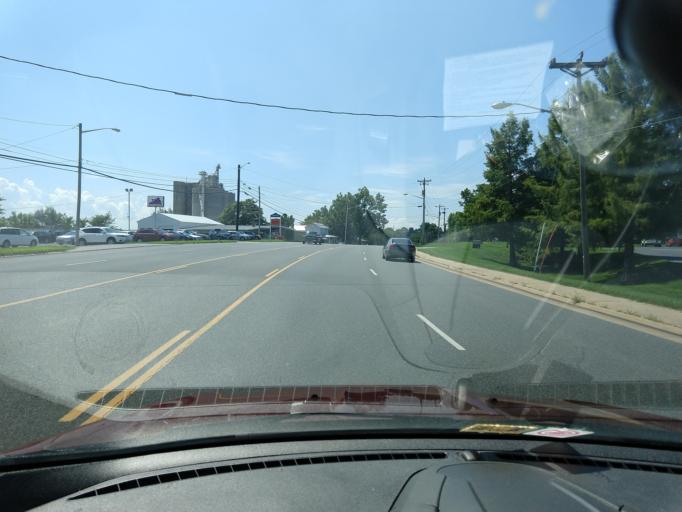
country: US
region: Virginia
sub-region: City of Harrisonburg
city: Harrisonburg
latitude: 38.4741
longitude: -78.8717
